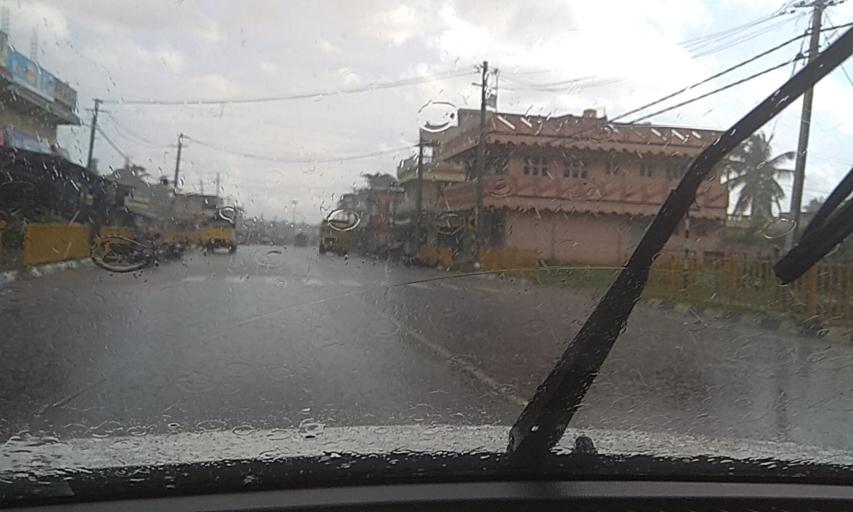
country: IN
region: Karnataka
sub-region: Mandya
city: Maddur
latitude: 12.6941
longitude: 77.0605
